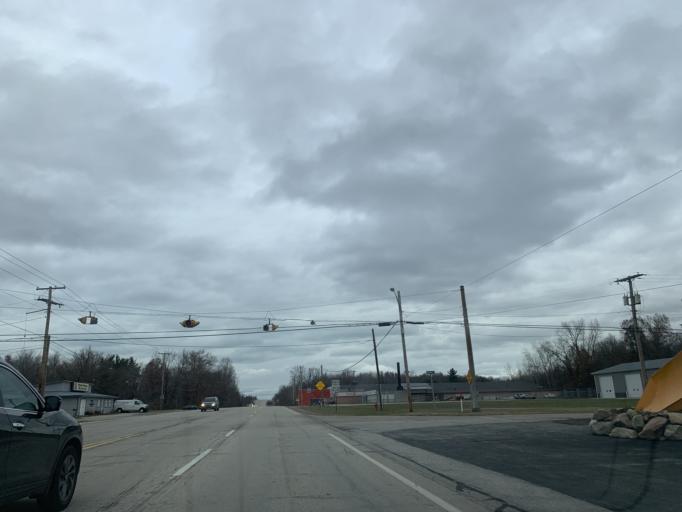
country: US
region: Indiana
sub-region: LaPorte County
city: Trail Creek
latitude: 41.7087
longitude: -86.8259
